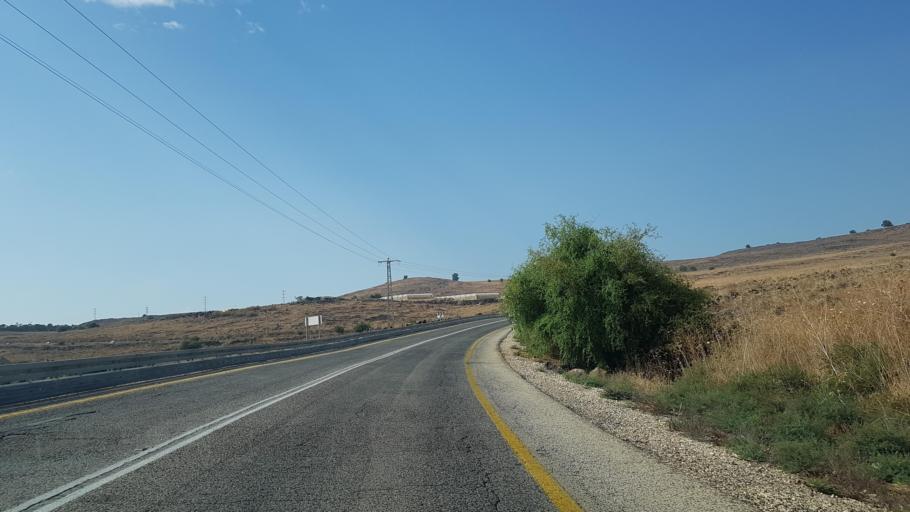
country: SY
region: Quneitra
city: Al Butayhah
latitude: 32.9119
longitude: 35.5920
